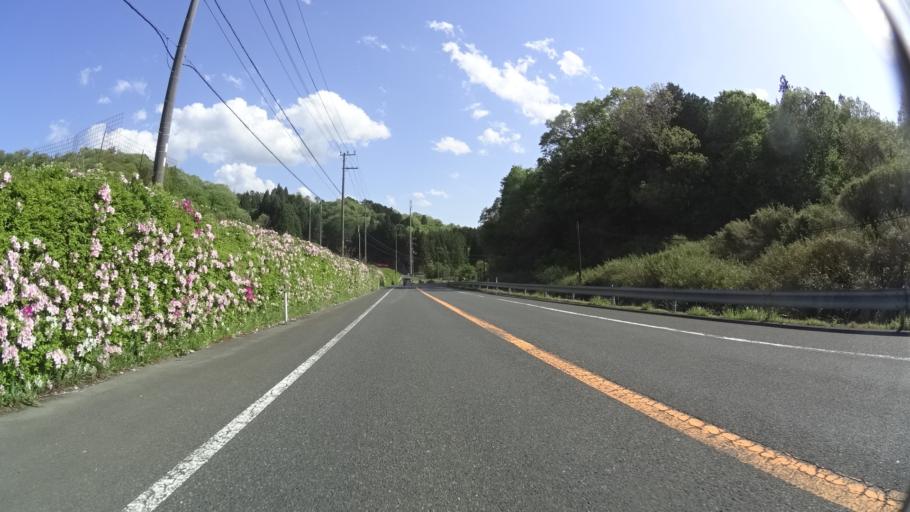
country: JP
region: Kyoto
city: Miyazu
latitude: 35.5548
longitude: 135.1121
